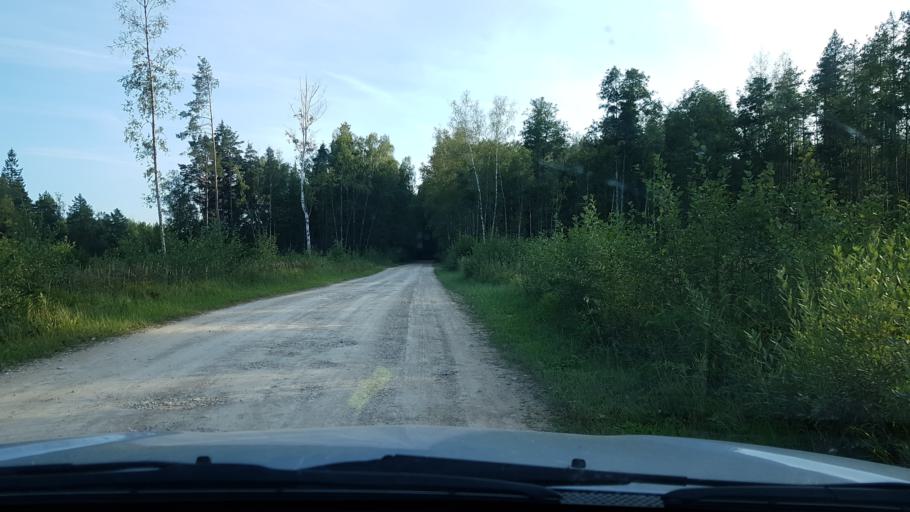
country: EE
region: Ida-Virumaa
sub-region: Sillamaee linn
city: Sillamae
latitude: 59.2673
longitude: 27.9236
